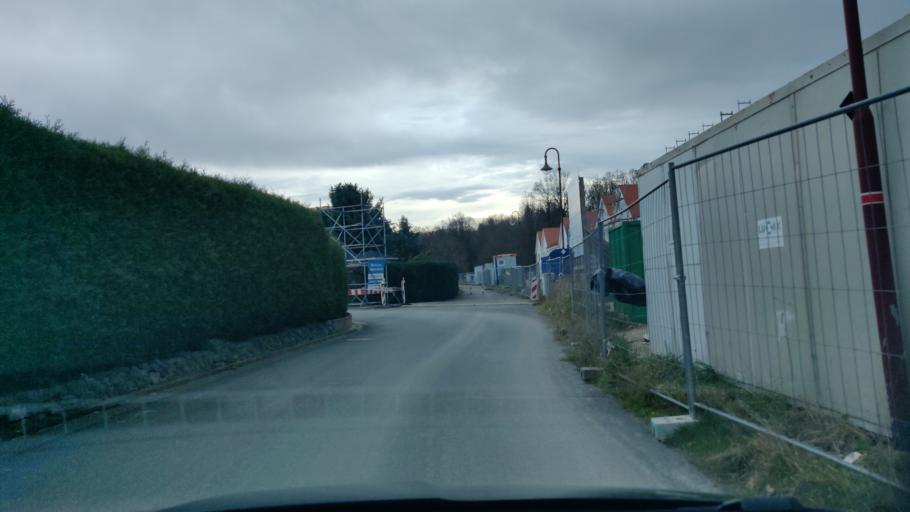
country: DE
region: Saxony
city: Bad Lausick
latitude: 51.1534
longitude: 12.6514
